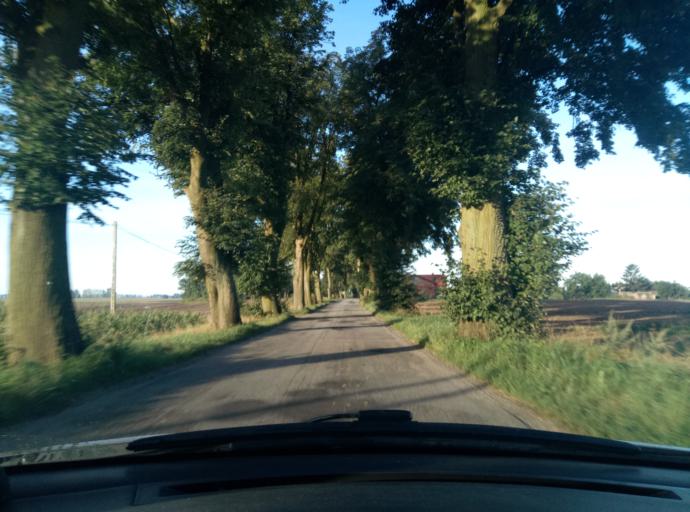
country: PL
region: Kujawsko-Pomorskie
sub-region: Powiat brodnicki
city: Jablonowo Pomorskie
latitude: 53.4154
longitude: 19.1785
